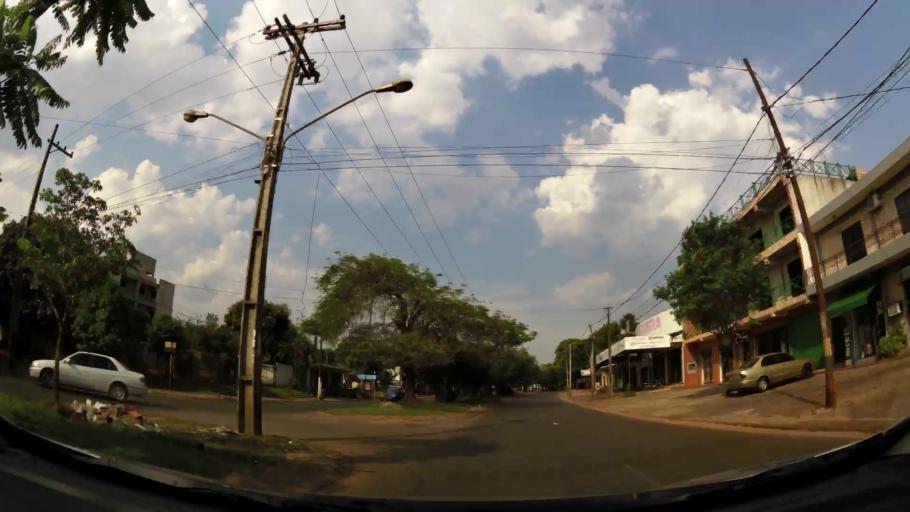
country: PY
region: Alto Parana
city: Presidente Franco
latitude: -25.5276
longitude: -54.6206
